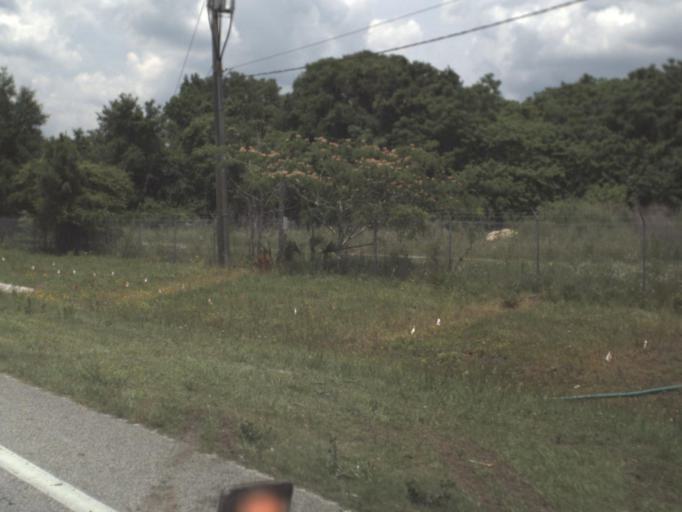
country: US
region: Florida
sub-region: Columbia County
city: Watertown
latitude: 30.1726
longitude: -82.5840
